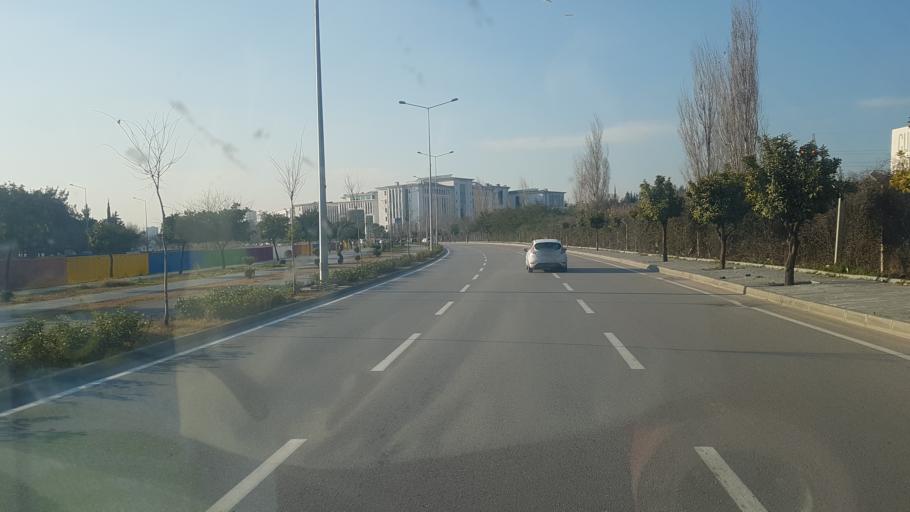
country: TR
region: Adana
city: Adana
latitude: 37.0120
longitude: 35.3514
